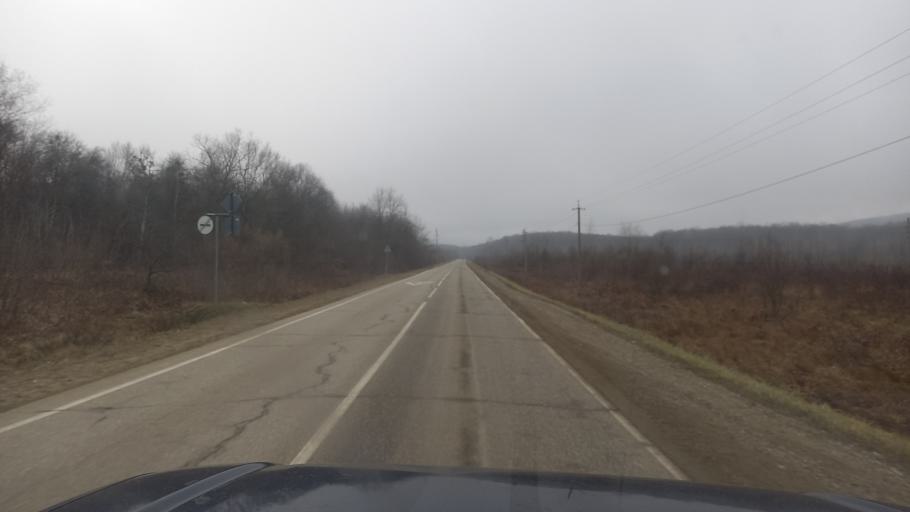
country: RU
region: Krasnodarskiy
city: Neftegorsk
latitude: 44.2888
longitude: 39.8133
